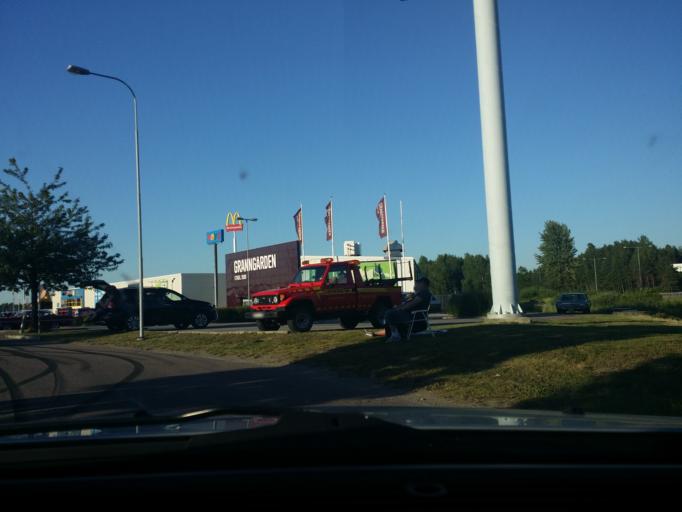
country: SE
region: Vaestmanland
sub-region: Vasteras
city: Vasteras
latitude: 59.6078
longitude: 16.6225
